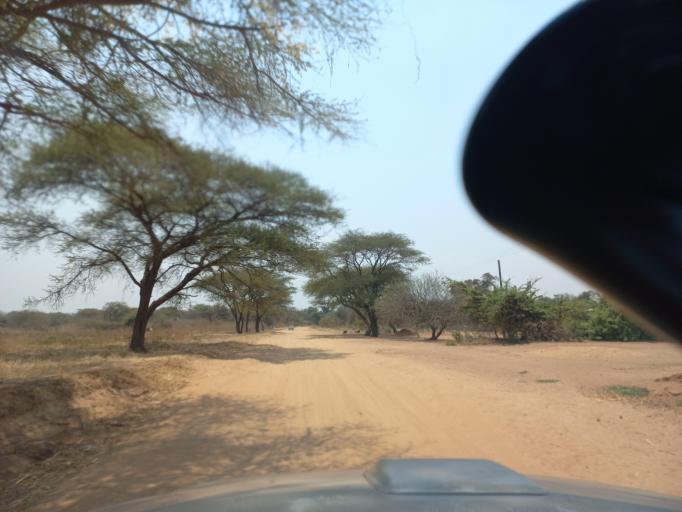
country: ZW
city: Chirundu
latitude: -15.9358
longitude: 28.8721
